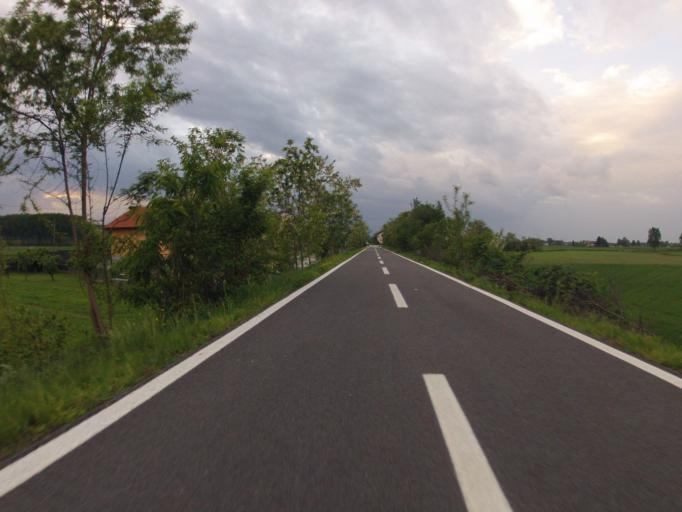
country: IT
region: Piedmont
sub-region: Provincia di Torino
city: Vigone
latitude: 44.8150
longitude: 7.4984
